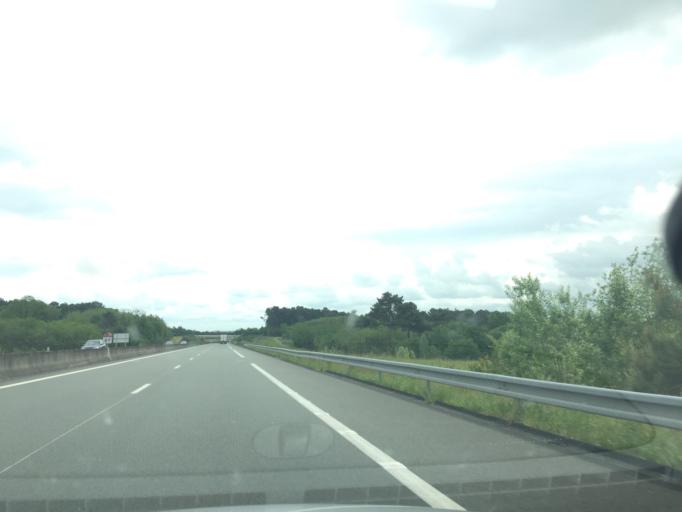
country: FR
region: Pays de la Loire
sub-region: Departement de la Sarthe
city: Luceau
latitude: 47.7001
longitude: 0.3545
